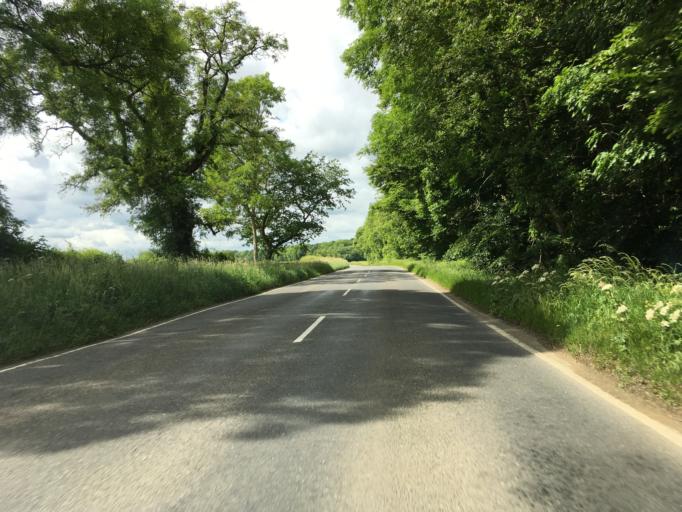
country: GB
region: England
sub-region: Oxfordshire
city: Chipping Norton
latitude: 51.9156
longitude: -1.5471
